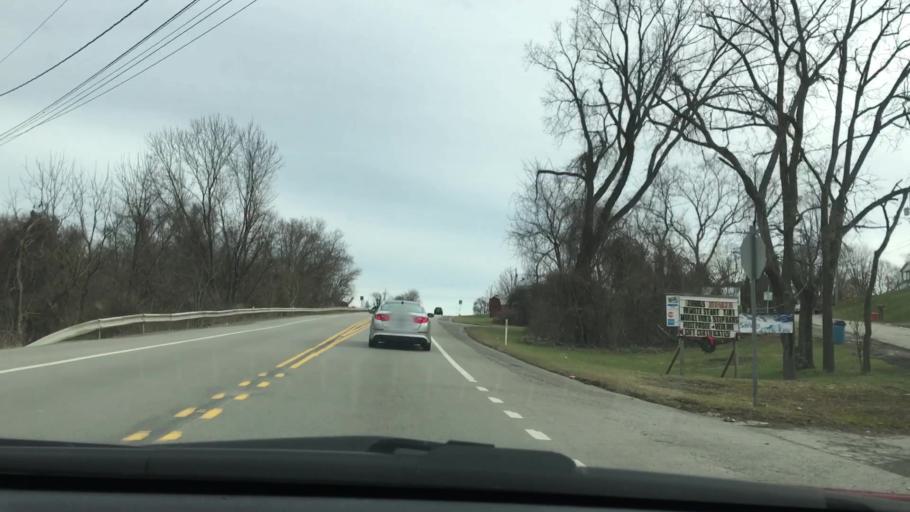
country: US
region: Pennsylvania
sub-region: Fayette County
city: Masontown
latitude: 39.8921
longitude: -79.8469
